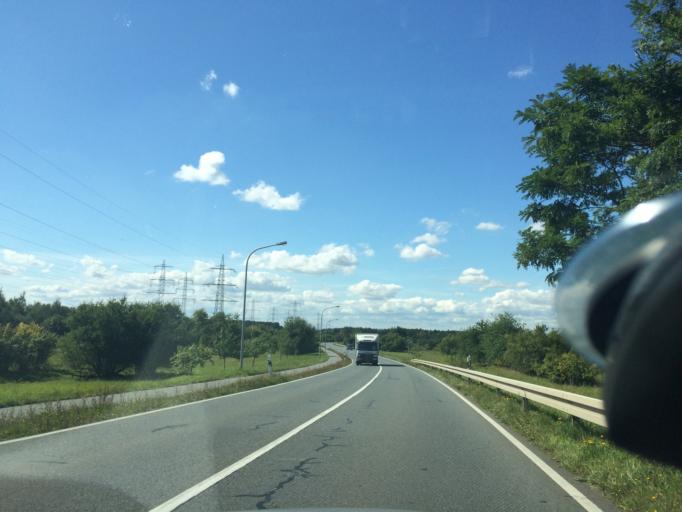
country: DE
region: Hesse
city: Morfelden-Walldorf
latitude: 49.9910
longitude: 8.5713
